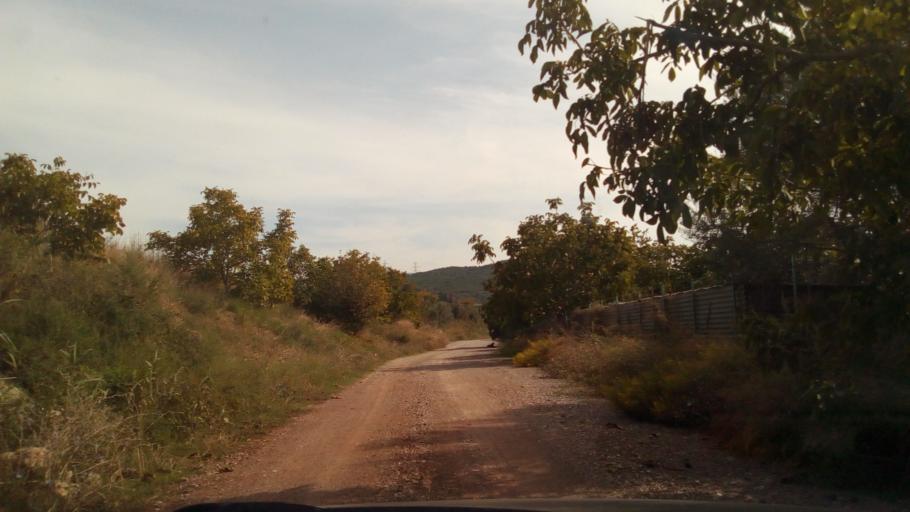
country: GR
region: West Greece
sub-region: Nomos Aitolias kai Akarnanias
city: Nafpaktos
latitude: 38.4102
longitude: 21.8903
